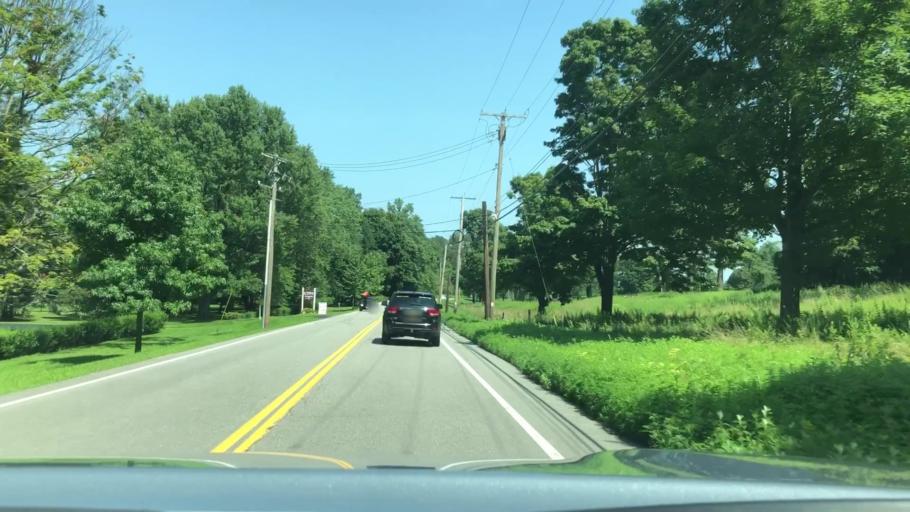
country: US
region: New York
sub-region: Orange County
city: Highland Falls
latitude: 41.3594
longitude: -73.9522
